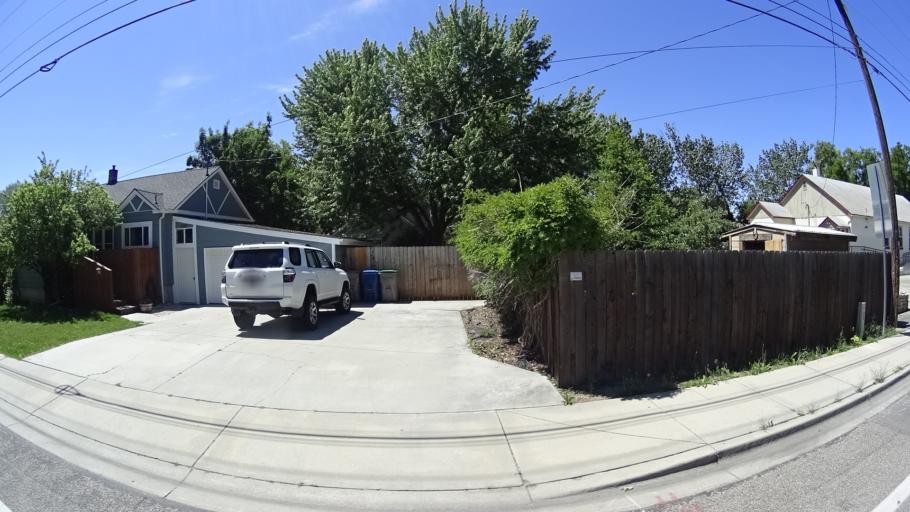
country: US
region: Idaho
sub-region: Ada County
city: Boise
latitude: 43.5779
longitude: -116.1721
